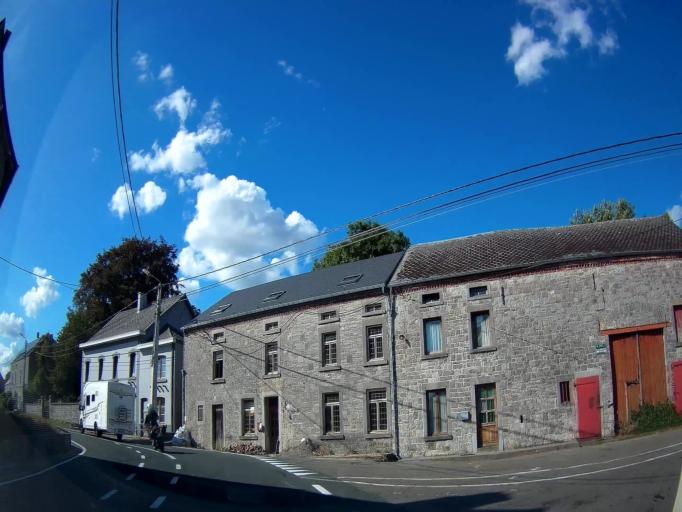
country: BE
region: Wallonia
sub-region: Province de Namur
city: Mettet
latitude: 50.3177
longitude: 4.7553
